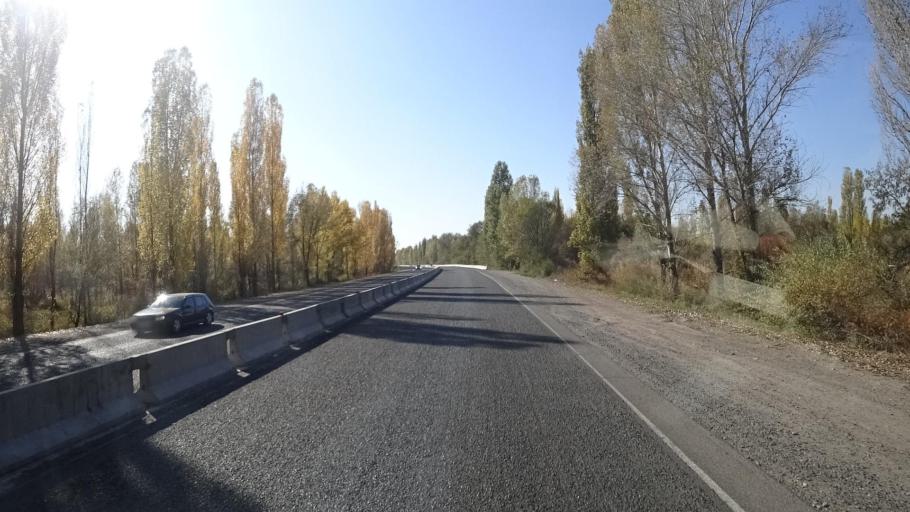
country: KG
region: Chuy
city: Tokmok
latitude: 42.8586
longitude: 75.2626
